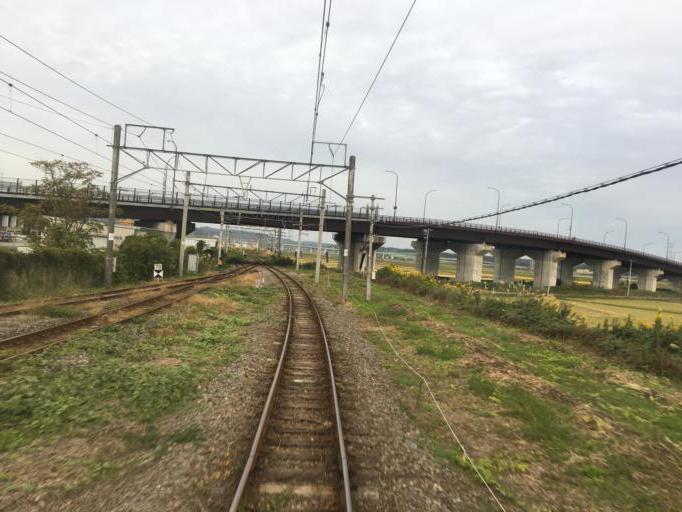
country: JP
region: Miyagi
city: Rifu
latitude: 38.3022
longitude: 140.9586
